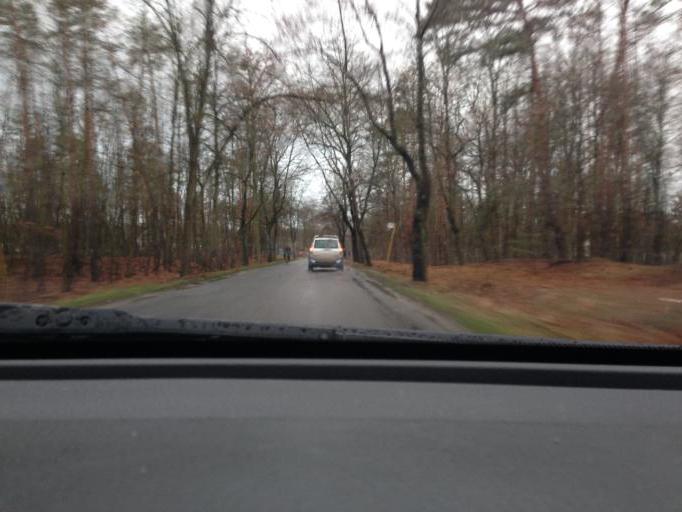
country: PL
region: Opole Voivodeship
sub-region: Powiat opolski
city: Wegry
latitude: 50.7228
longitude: 18.0197
